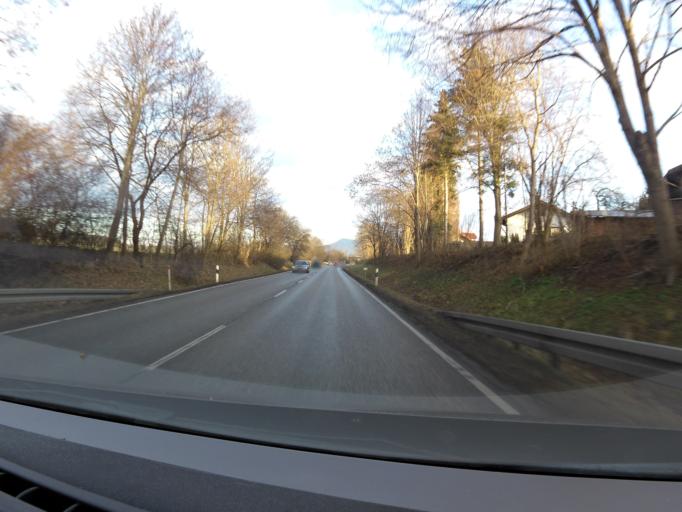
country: DE
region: Bavaria
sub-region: Upper Bavaria
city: Sindelsdorf
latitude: 47.7275
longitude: 11.3311
